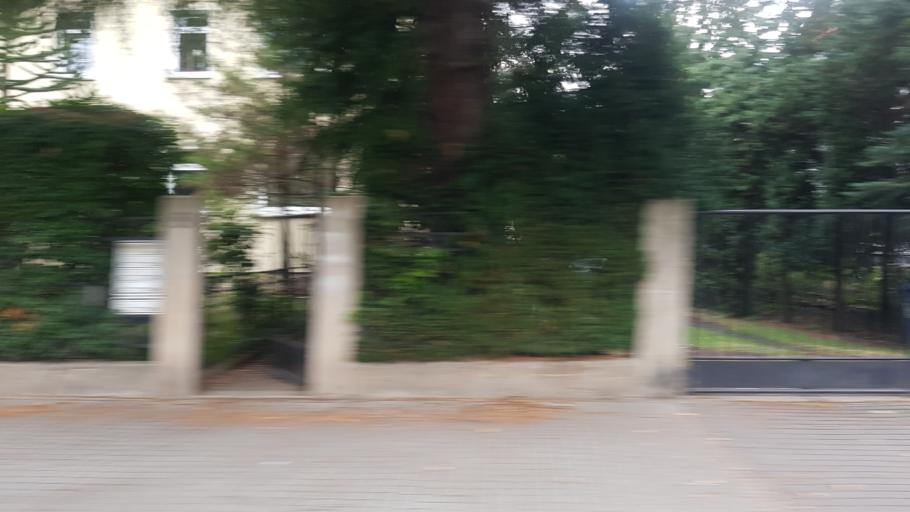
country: DE
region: Saxony
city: Heidenau
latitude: 51.0263
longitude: 13.8310
